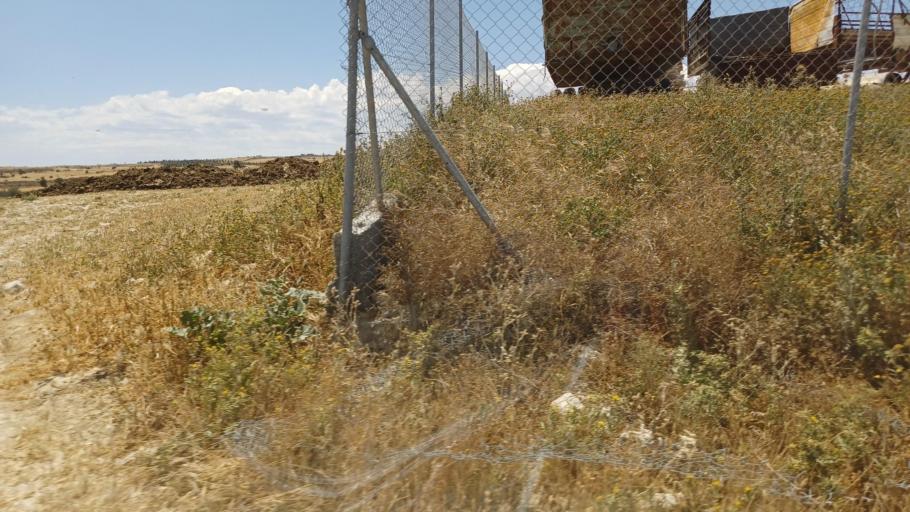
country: CY
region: Larnaka
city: Athienou
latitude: 35.0371
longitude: 33.5404
